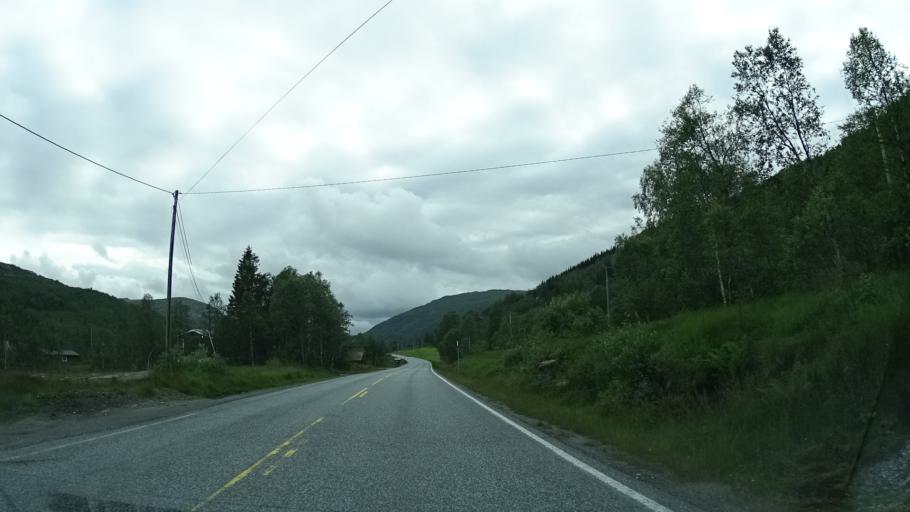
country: NO
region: Hordaland
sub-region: Samnanger
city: Tysse
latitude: 60.3938
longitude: 5.9440
